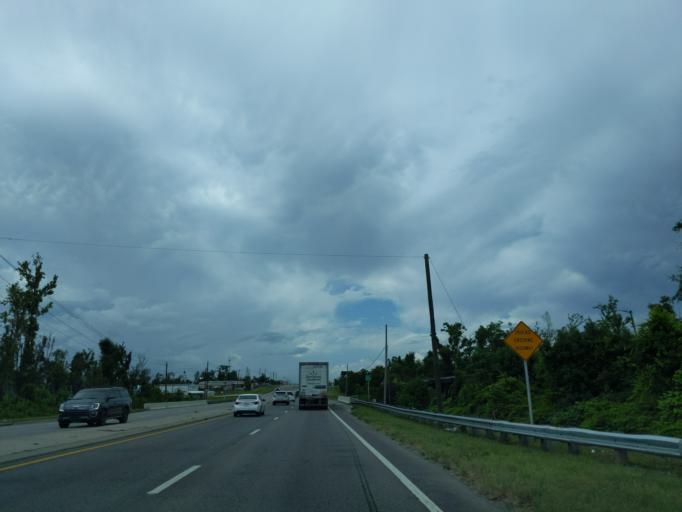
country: US
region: Florida
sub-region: Bay County
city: Hiland Park
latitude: 30.2181
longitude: -85.6001
